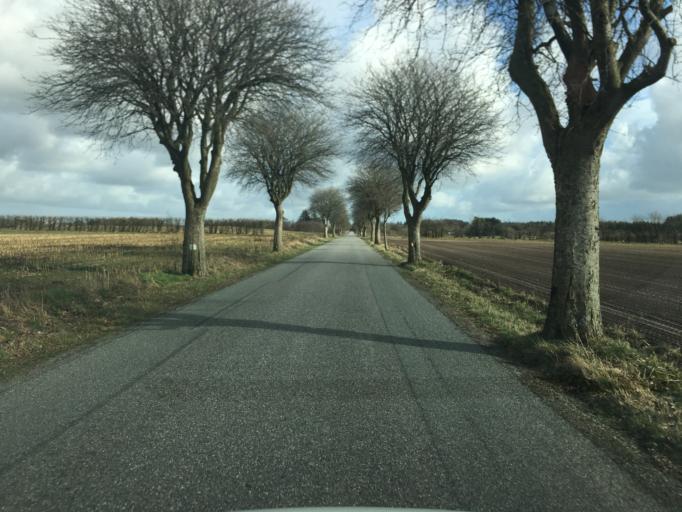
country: DK
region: South Denmark
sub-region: Aabenraa Kommune
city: Krusa
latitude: 54.9017
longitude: 9.3934
